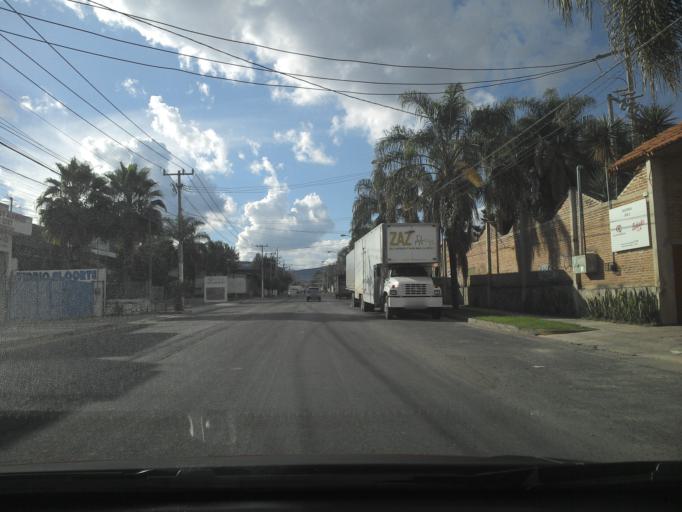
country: MX
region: Jalisco
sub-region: Tlajomulco de Zuniga
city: Palomar
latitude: 20.6153
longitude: -103.4405
